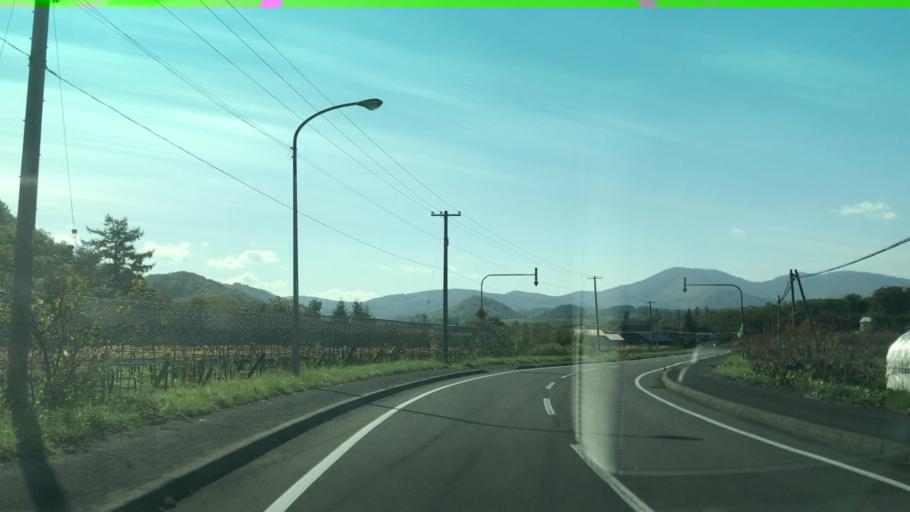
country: JP
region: Hokkaido
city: Yoichi
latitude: 43.1711
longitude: 140.8216
